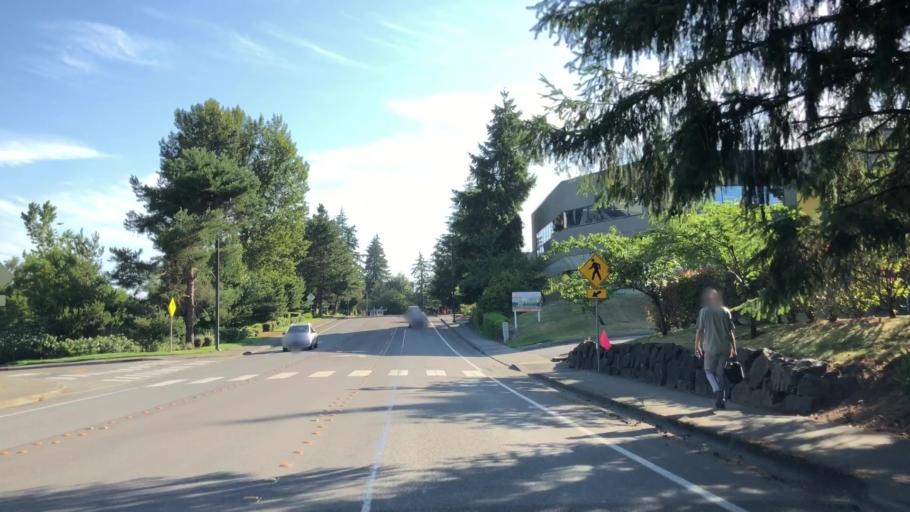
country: US
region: Washington
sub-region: King County
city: Eastgate
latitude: 47.5819
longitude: -122.1295
